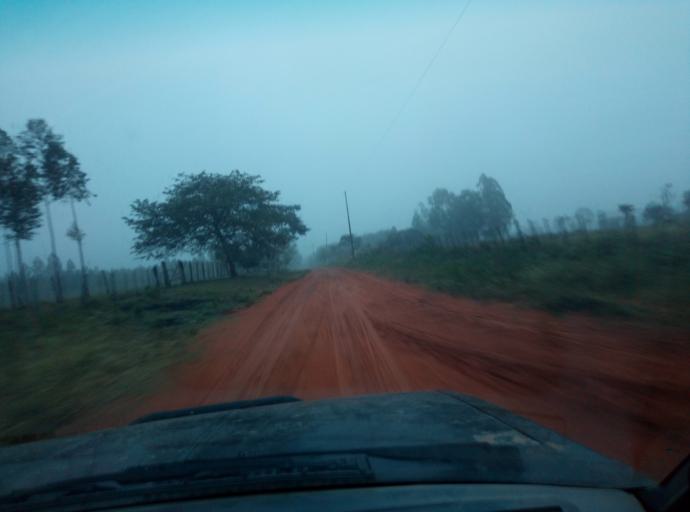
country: PY
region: Caaguazu
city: Doctor Cecilio Baez
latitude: -25.1551
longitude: -56.2874
